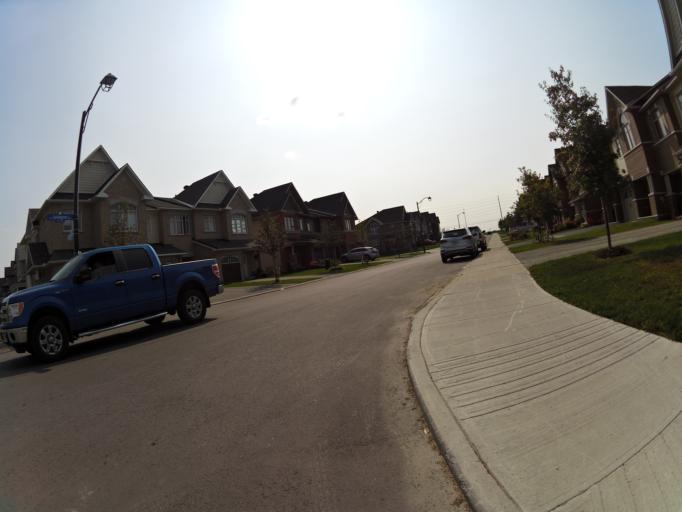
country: CA
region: Ontario
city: Bells Corners
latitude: 45.3037
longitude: -75.9362
